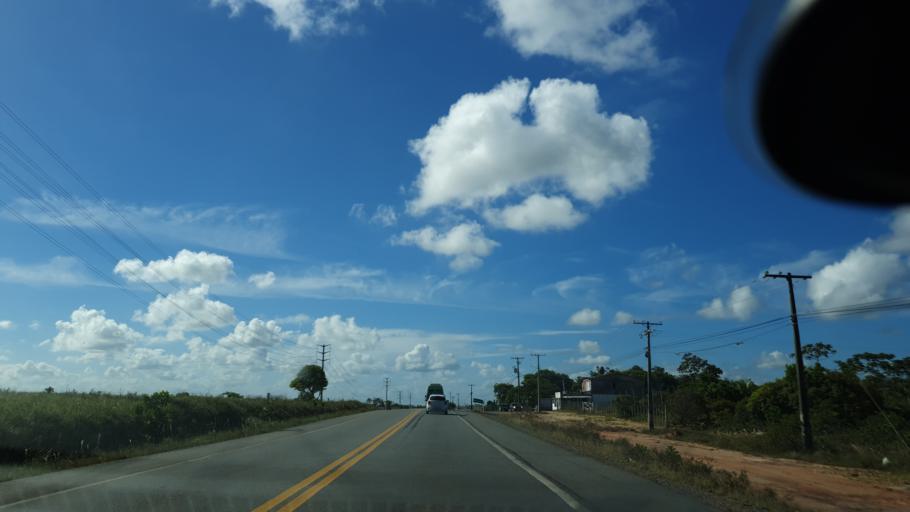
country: BR
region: Bahia
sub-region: Camacari
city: Camacari
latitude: -12.7006
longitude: -38.2165
